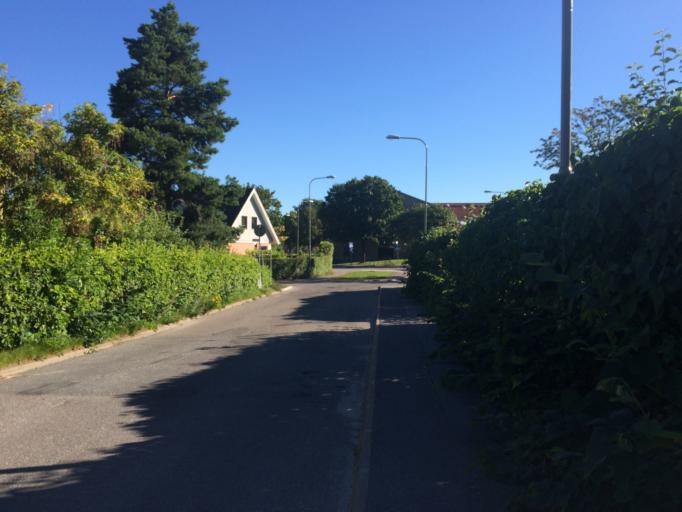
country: SE
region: Stockholm
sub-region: Stockholms Kommun
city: Kista
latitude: 59.3793
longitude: 17.8907
